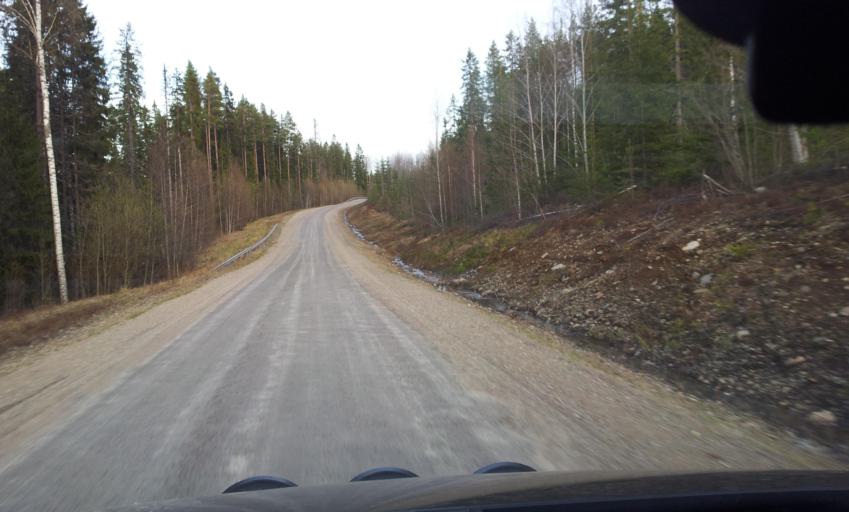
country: SE
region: Gaevleborg
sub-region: Ljusdals Kommun
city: Farila
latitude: 62.1085
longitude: 15.7255
